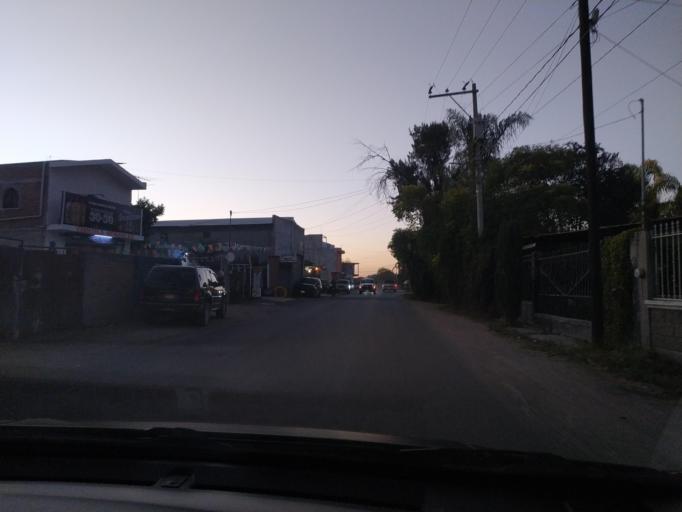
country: MX
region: Guanajuato
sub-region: San Francisco del Rincon
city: San Roque de Montes
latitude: 21.0156
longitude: -101.8154
